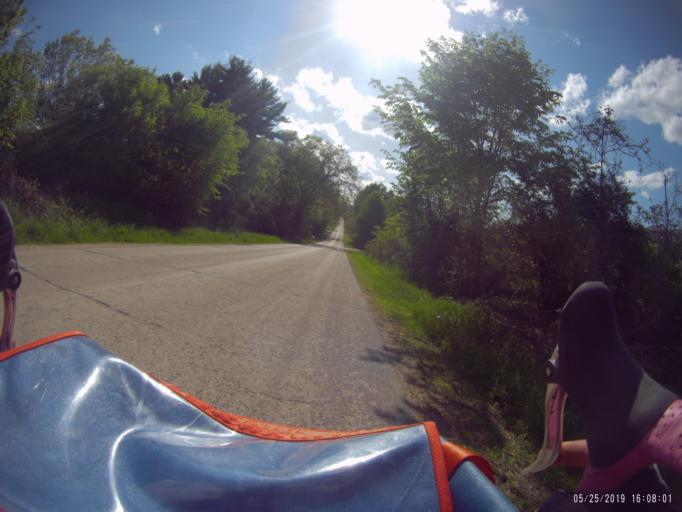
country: US
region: Wisconsin
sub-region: Dane County
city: Mount Horeb
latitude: 42.9626
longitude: -89.6487
